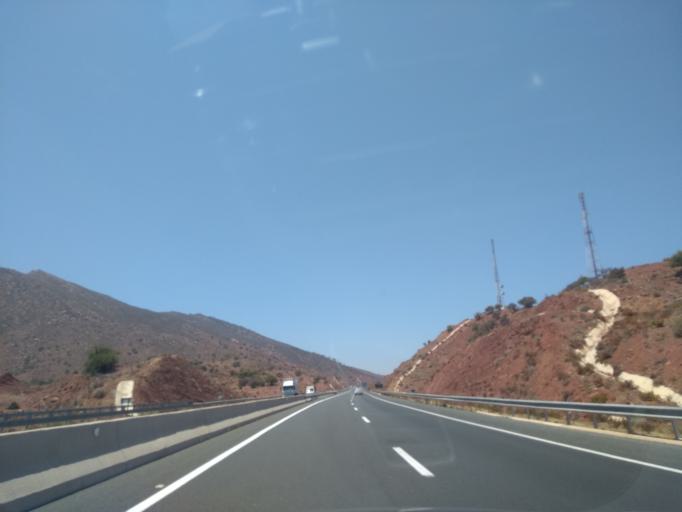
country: MA
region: Souss-Massa-Draa
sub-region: Taroudannt
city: Bigoudine
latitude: 30.6661
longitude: -9.2483
